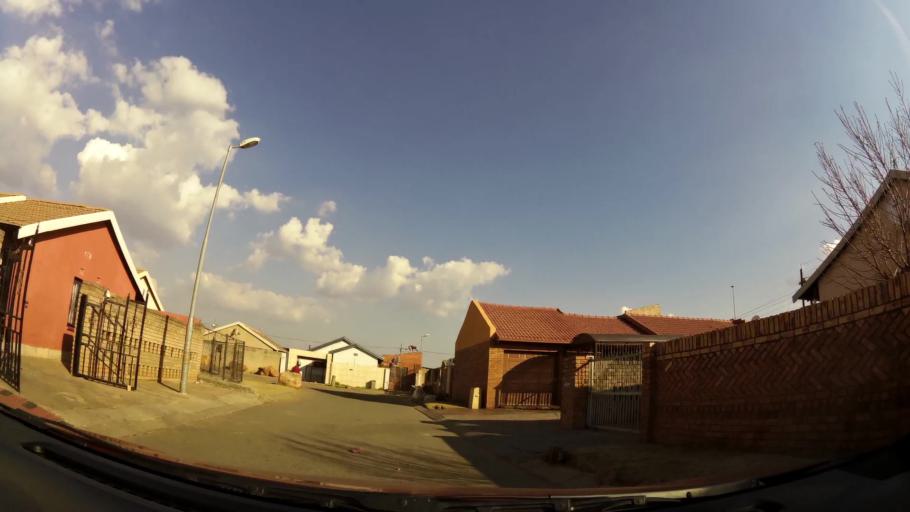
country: ZA
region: Gauteng
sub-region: City of Johannesburg Metropolitan Municipality
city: Soweto
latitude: -26.2312
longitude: 27.8590
